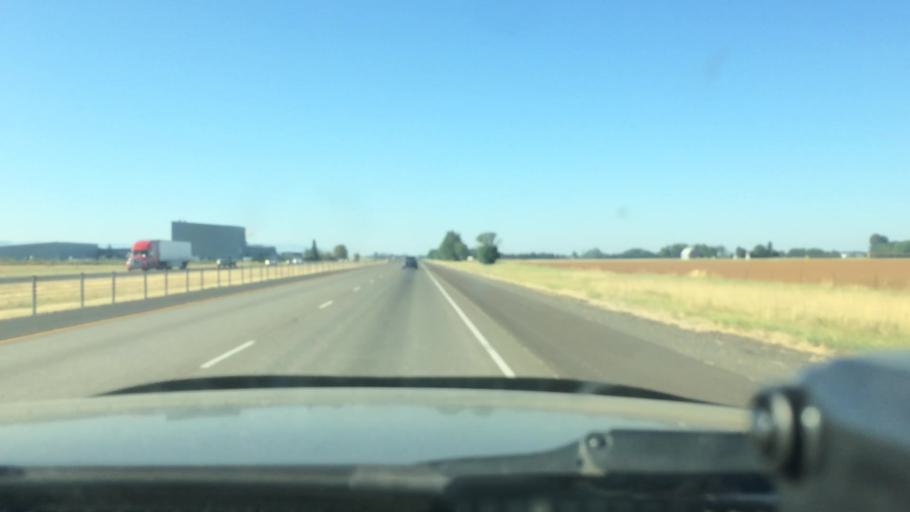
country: US
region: Oregon
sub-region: Linn County
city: Tangent
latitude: 44.5743
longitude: -123.0621
